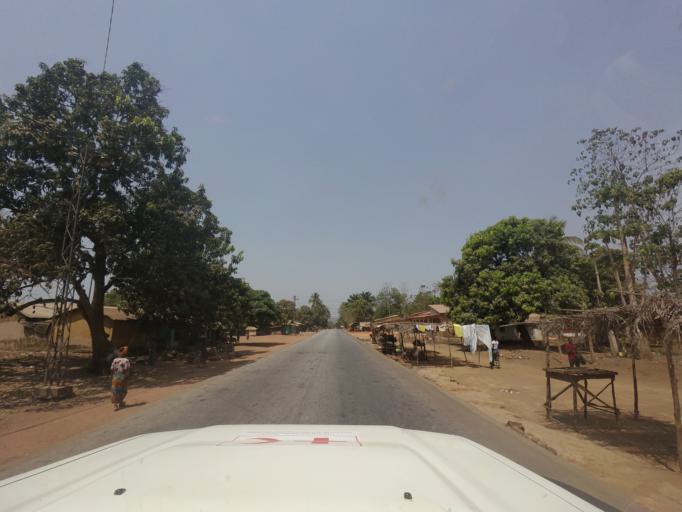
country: GN
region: Kindia
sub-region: Kindia
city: Kindia
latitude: 9.9497
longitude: -12.9518
